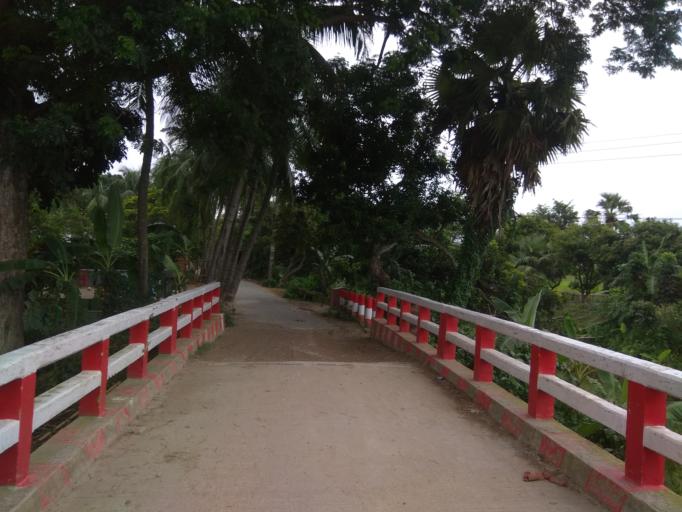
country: BD
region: Dhaka
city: Dohar
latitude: 23.4860
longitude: 90.0263
